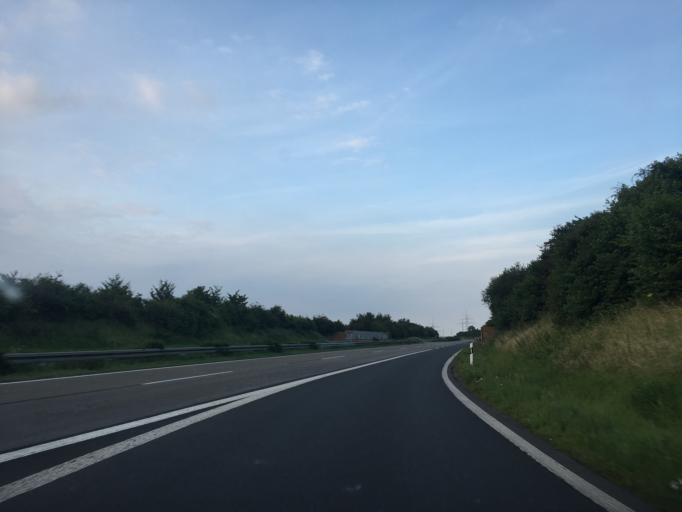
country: DE
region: North Rhine-Westphalia
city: Huckelhoven
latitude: 51.0596
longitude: 6.1913
